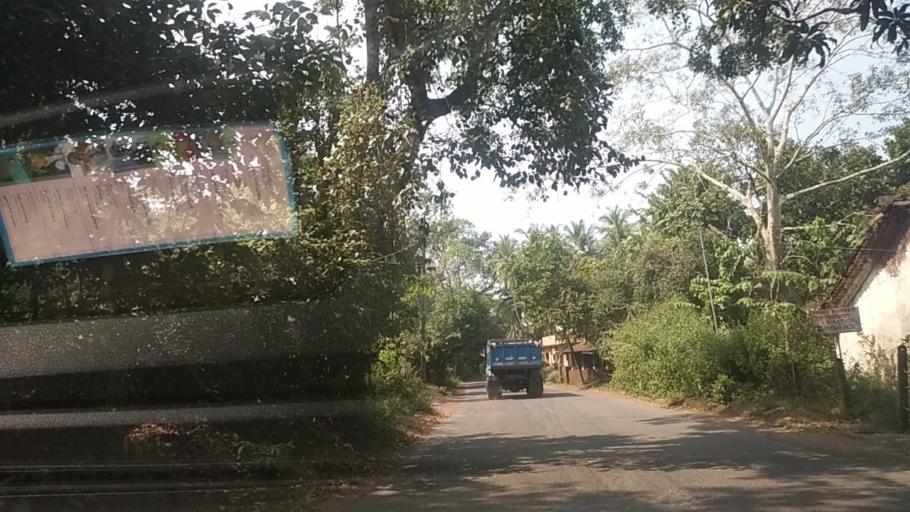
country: IN
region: Goa
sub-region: North Goa
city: Solim
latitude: 15.6162
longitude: 73.7901
